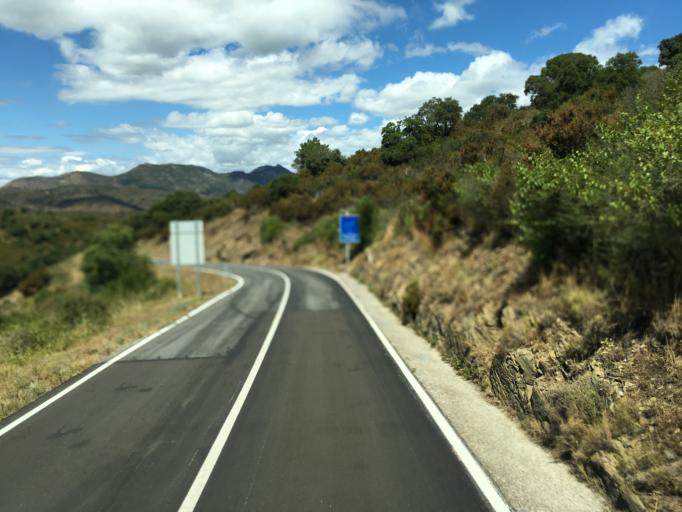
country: ES
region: Catalonia
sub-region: Provincia de Girona
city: Cadaques
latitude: 42.2980
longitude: 3.2353
